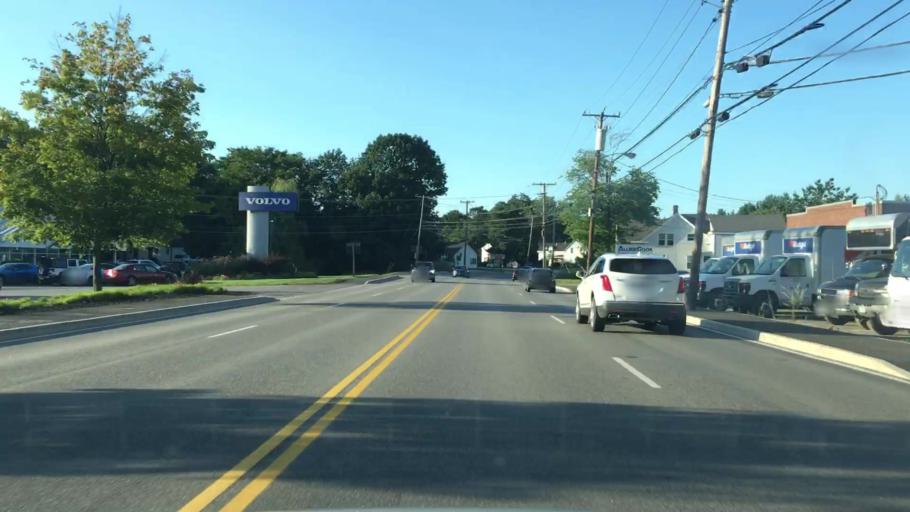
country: US
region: Maine
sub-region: Cumberland County
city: South Portland Gardens
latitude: 43.6123
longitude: -70.3128
